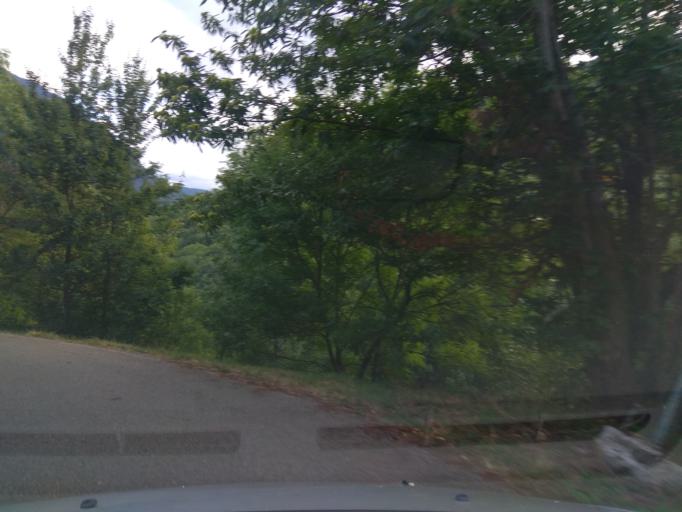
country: ES
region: Catalonia
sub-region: Provincia de Lleida
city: Les
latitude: 42.8327
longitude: 0.7180
